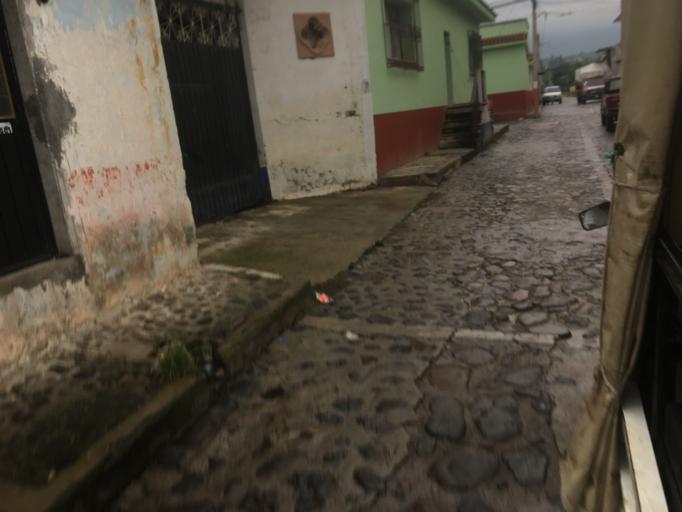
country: MX
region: Morelos
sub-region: Tlayacapan
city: Tlayacapan
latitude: 18.9569
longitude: -98.9867
